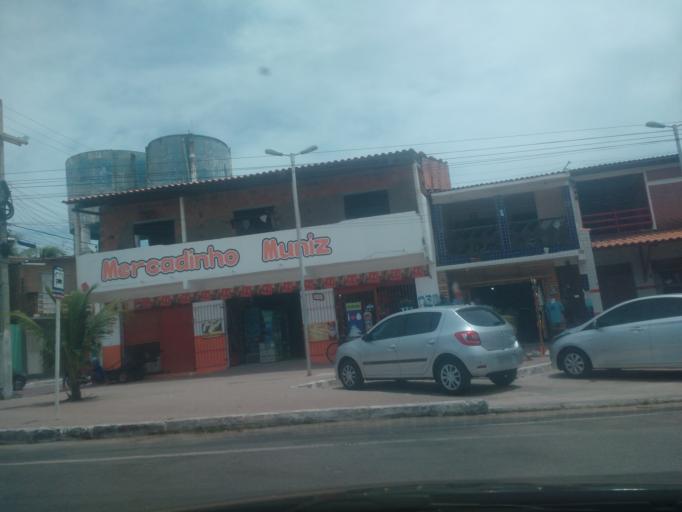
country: BR
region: Alagoas
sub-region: Marechal Deodoro
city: Marechal Deodoro
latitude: -9.7701
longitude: -35.8425
